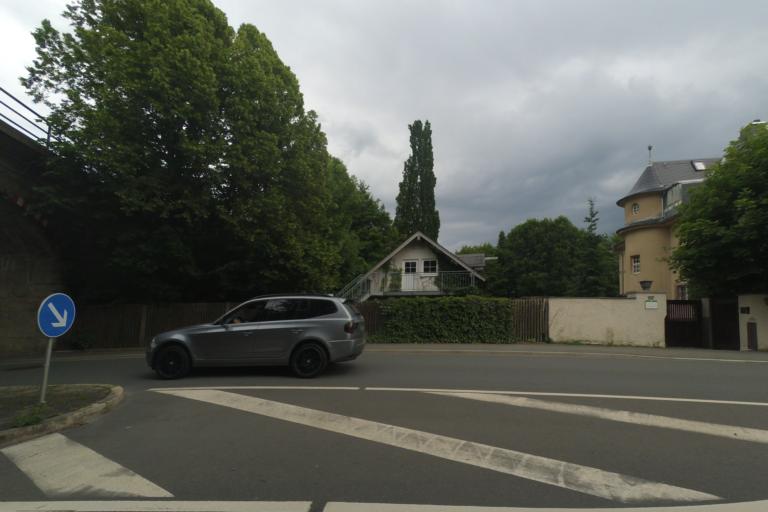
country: DE
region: Bavaria
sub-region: Upper Franconia
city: Munchberg
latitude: 50.1920
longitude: 11.7778
